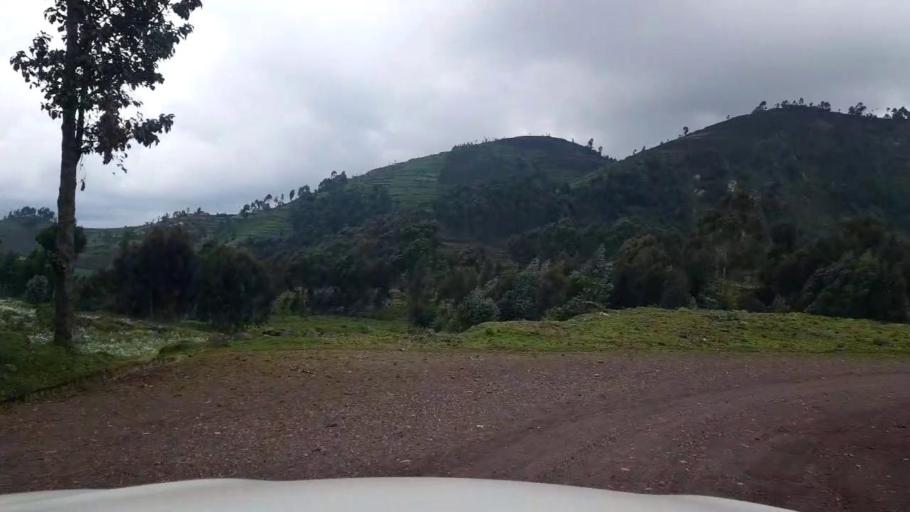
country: RW
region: Northern Province
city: Musanze
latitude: -1.5878
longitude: 29.4718
